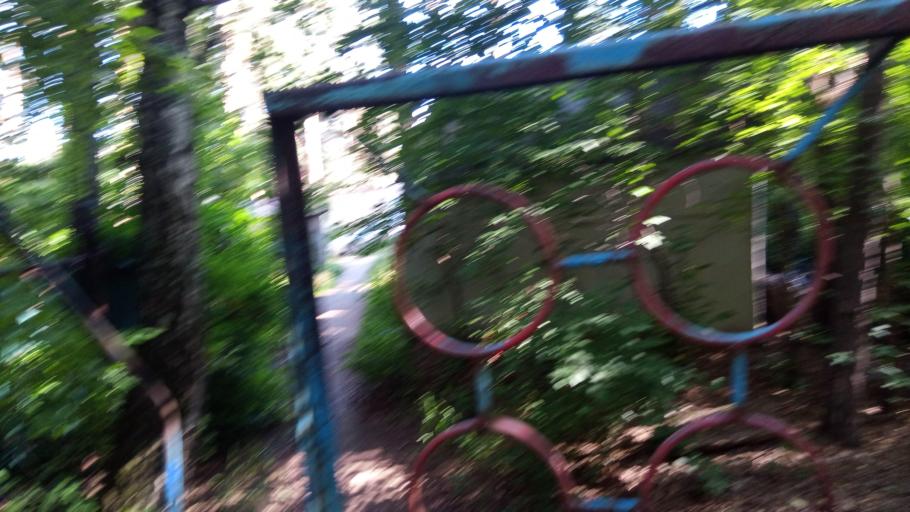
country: RU
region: Chelyabinsk
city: Chebarkul'
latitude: 55.0189
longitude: 60.3157
